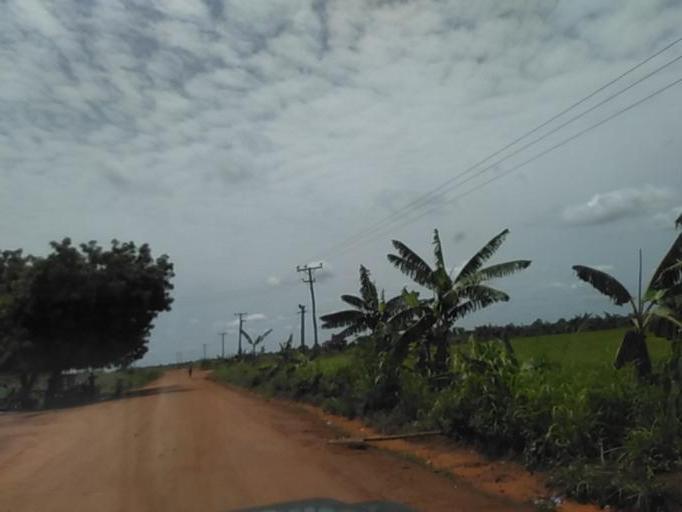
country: GH
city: Akropong
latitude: 6.0926
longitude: 0.2270
